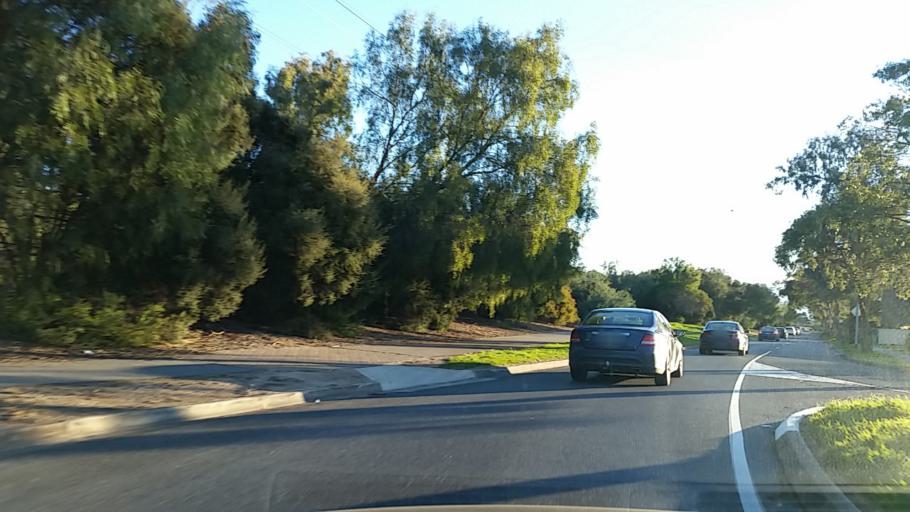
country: AU
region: South Australia
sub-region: Salisbury
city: Salisbury
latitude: -34.7592
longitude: 138.6286
